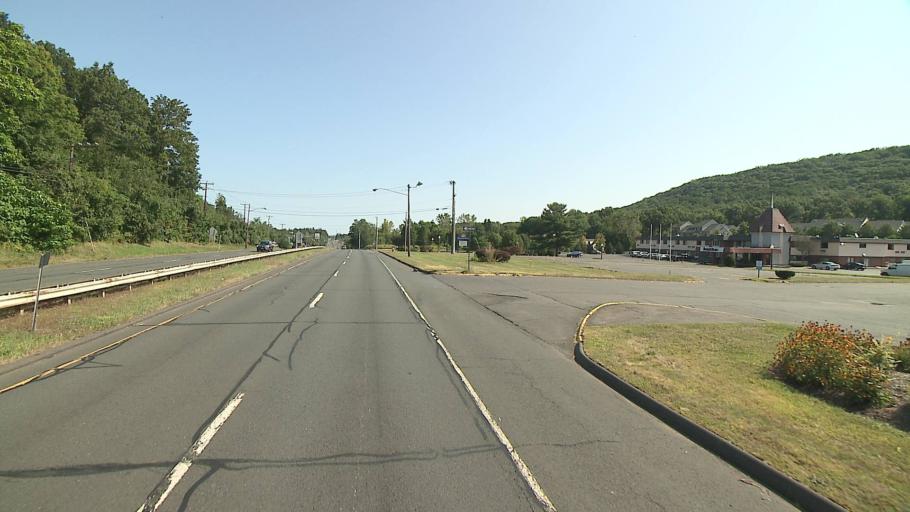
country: US
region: Connecticut
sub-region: Hartford County
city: Kensington
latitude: 41.5874
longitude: -72.7608
